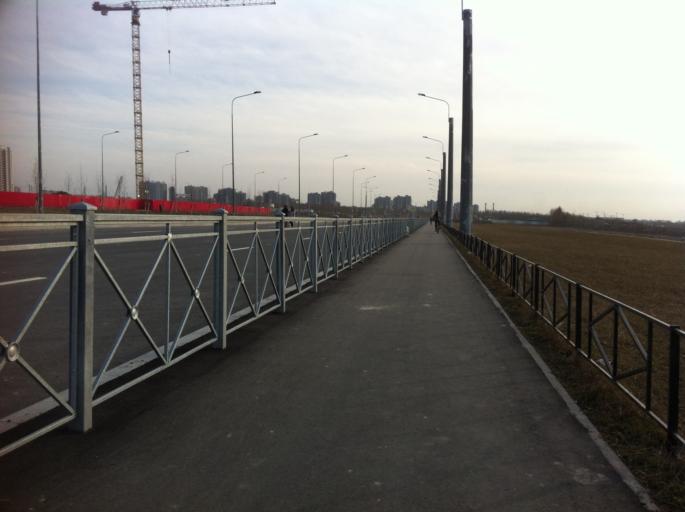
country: RU
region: St.-Petersburg
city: Sosnovaya Polyana
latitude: 59.8700
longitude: 30.1551
